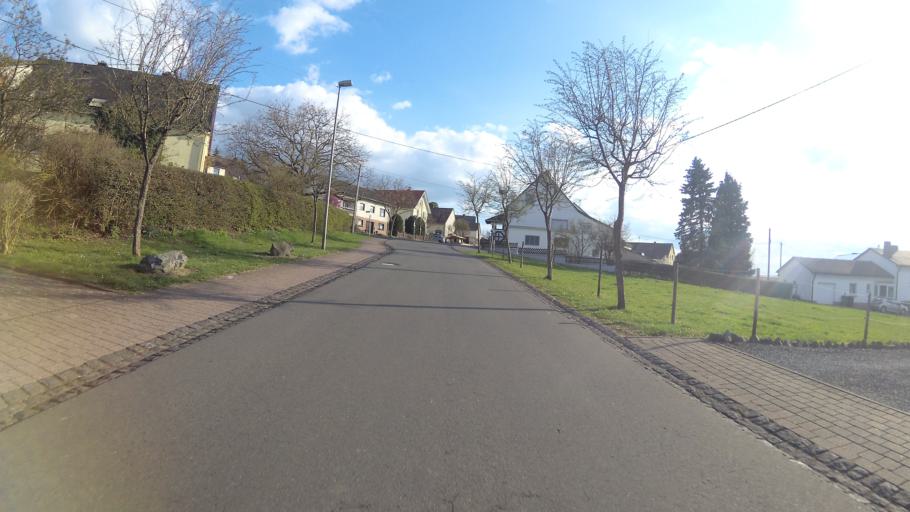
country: DE
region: Rheinland-Pfalz
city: Steiningen
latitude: 50.1811
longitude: 6.9147
